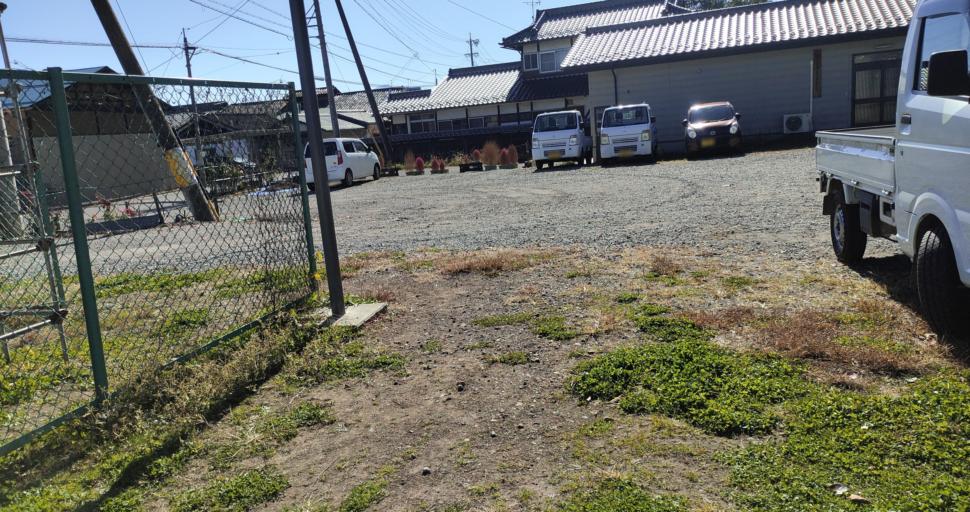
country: JP
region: Nagano
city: Saku
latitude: 36.2271
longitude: 138.4433
